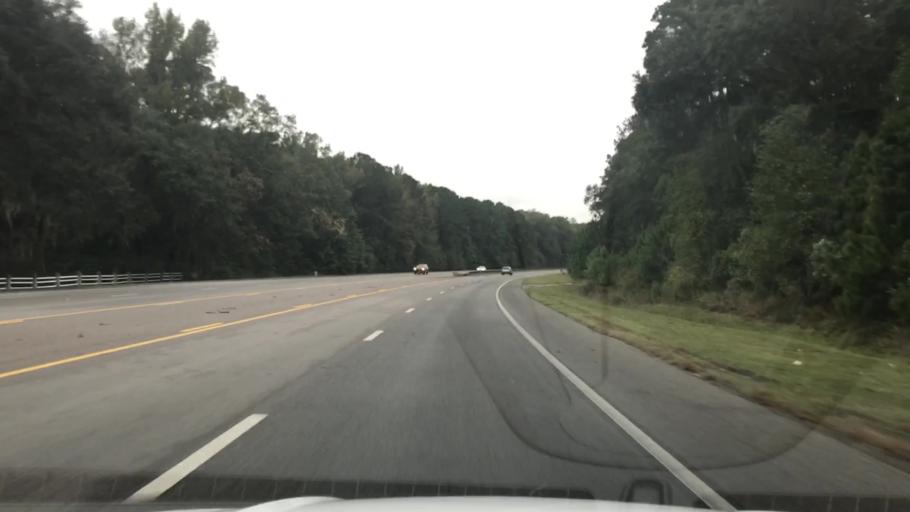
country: US
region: South Carolina
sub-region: Hampton County
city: Yemassee
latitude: 32.6644
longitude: -80.6537
